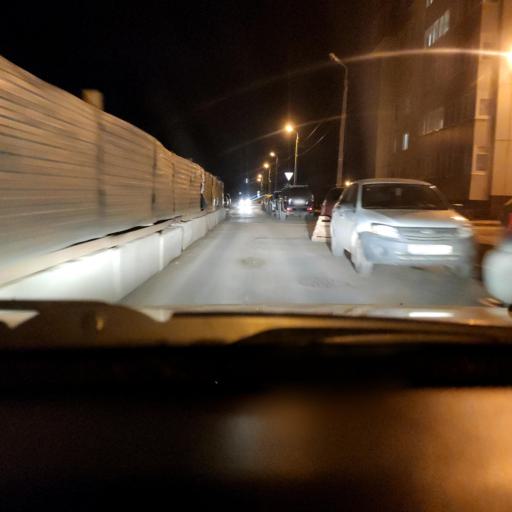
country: RU
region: Perm
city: Kondratovo
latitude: 57.9880
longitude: 56.1203
